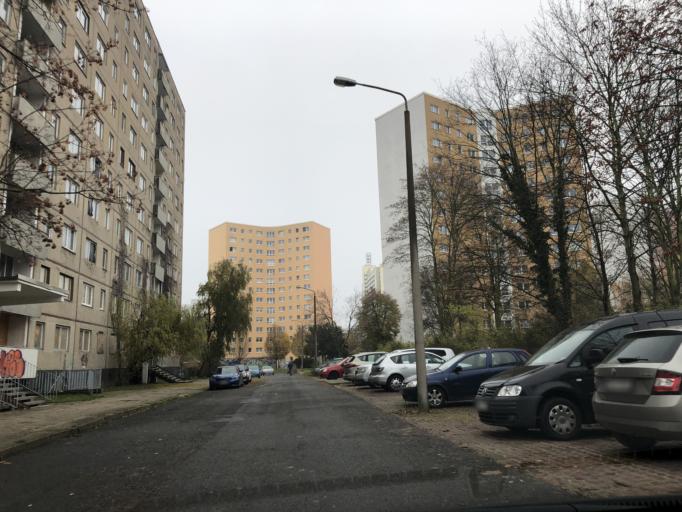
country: DE
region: Saxony-Anhalt
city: Halle Neustadt
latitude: 51.4846
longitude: 11.9256
